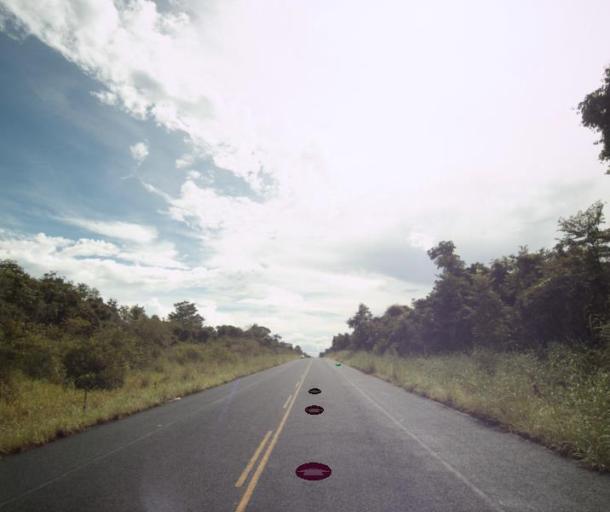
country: BR
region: Goias
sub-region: Sao Miguel Do Araguaia
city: Sao Miguel do Araguaia
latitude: -13.2987
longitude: -50.3215
